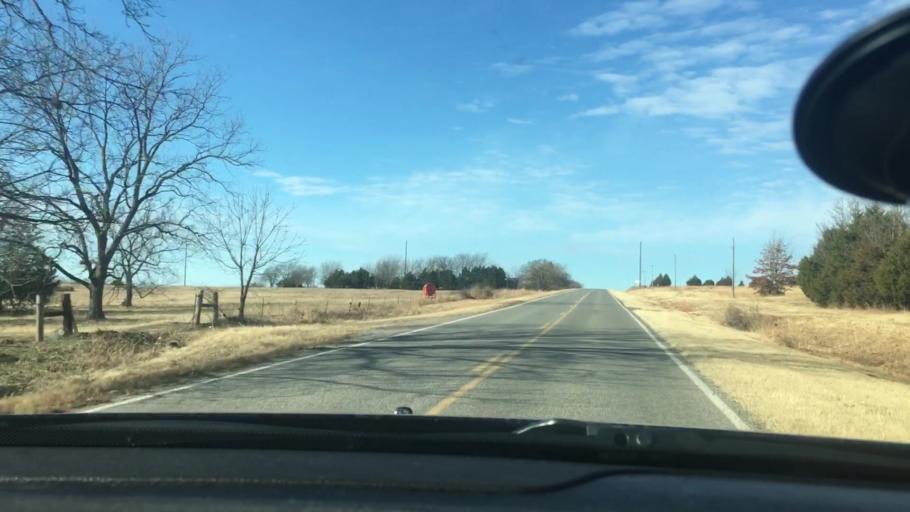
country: US
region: Oklahoma
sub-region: Seminole County
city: Konawa
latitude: 34.9856
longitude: -96.8052
